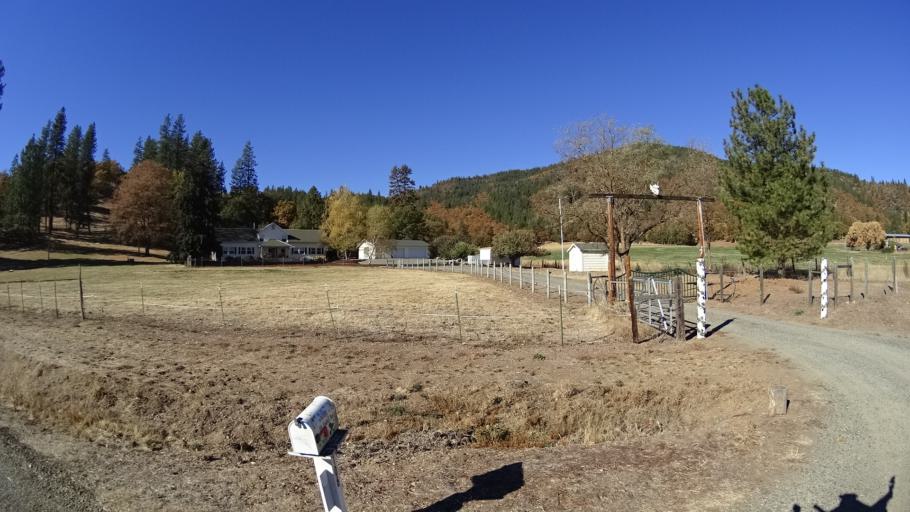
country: US
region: California
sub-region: Siskiyou County
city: Yreka
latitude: 41.5897
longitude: -122.8584
